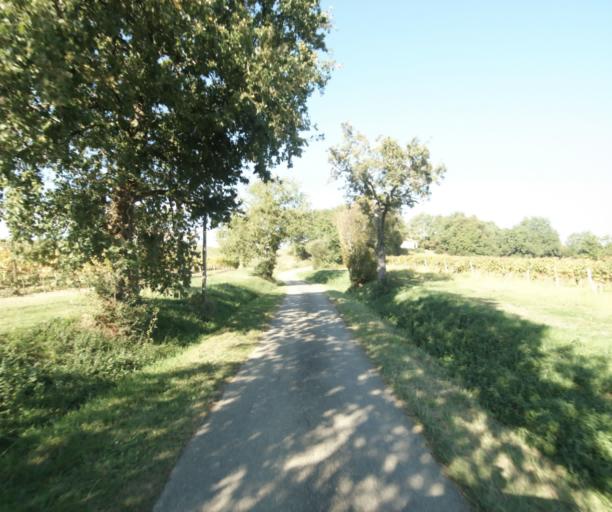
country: FR
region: Midi-Pyrenees
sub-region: Departement du Gers
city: Eauze
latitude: 43.8012
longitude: 0.1285
